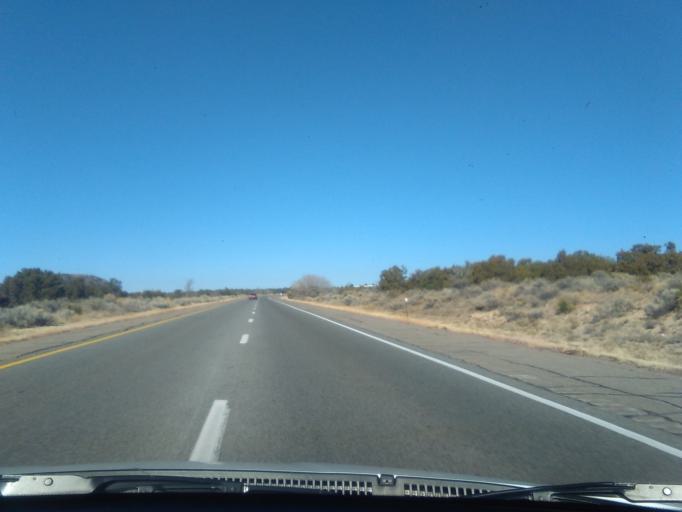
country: US
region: New Mexico
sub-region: Santa Fe County
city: Eldorado at Santa Fe
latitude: 35.5746
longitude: -105.8935
